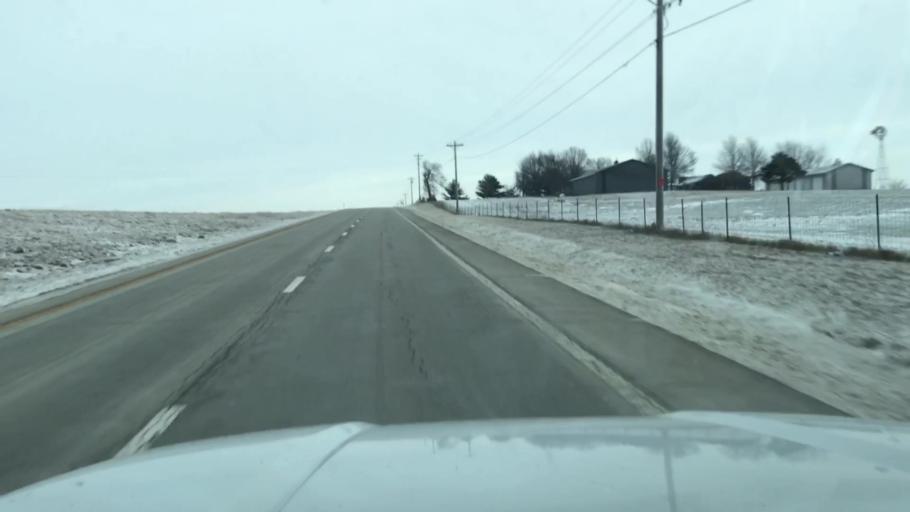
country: US
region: Missouri
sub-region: Andrew County
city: Savannah
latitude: 39.9908
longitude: -94.8799
